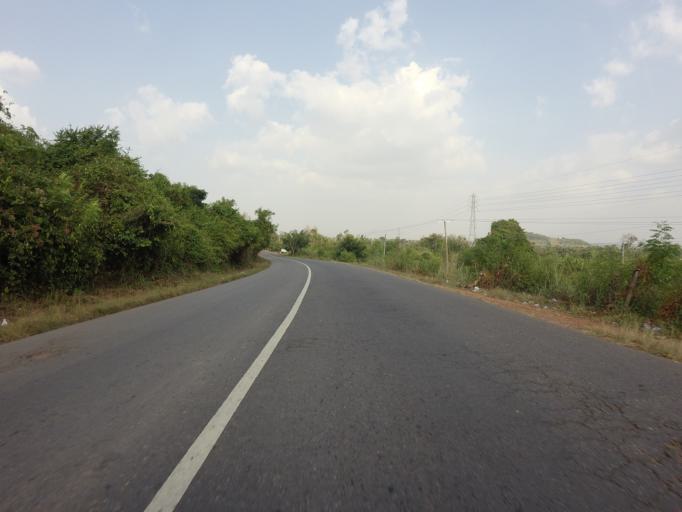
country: GH
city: Akropong
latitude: 6.2373
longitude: 0.1019
